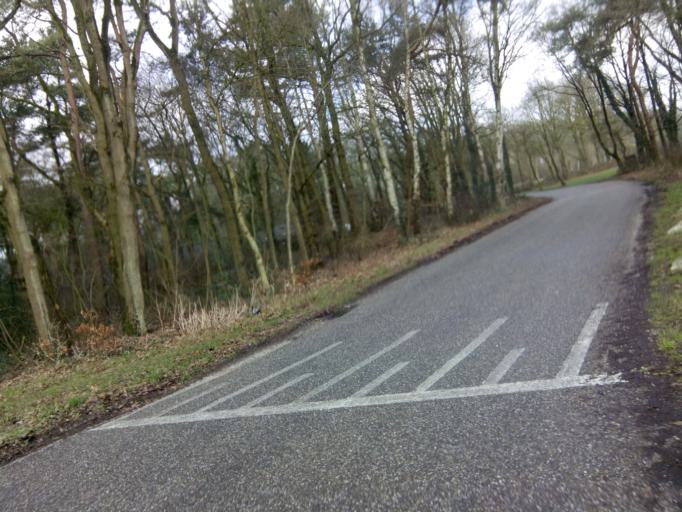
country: NL
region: Utrecht
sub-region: Gemeente Utrechtse Heuvelrug
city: Overberg
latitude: 52.0309
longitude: 5.4926
